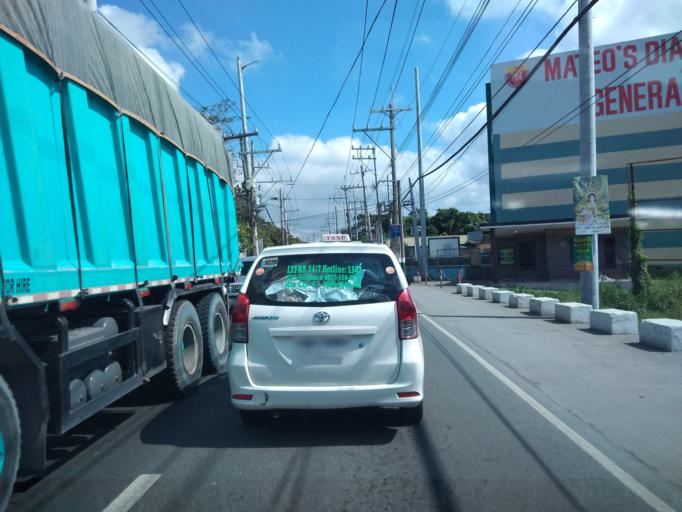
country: PH
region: Central Luzon
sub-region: Province of Bulacan
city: Santa Maria
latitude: 14.8094
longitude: 120.9471
